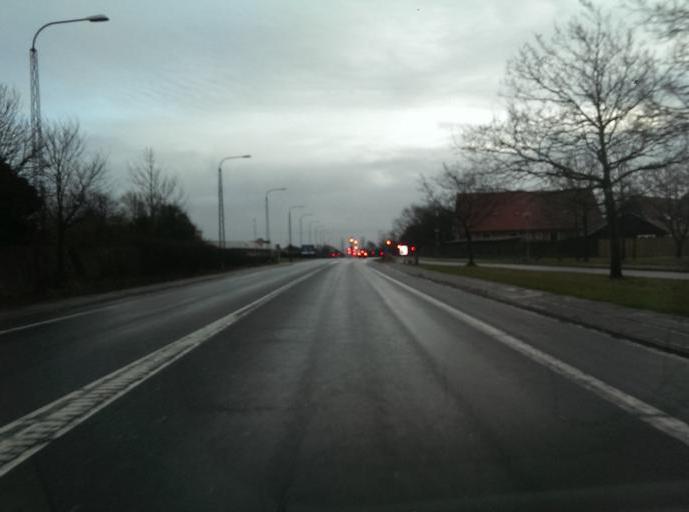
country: DK
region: South Denmark
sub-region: Esbjerg Kommune
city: Esbjerg
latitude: 55.5014
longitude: 8.4064
